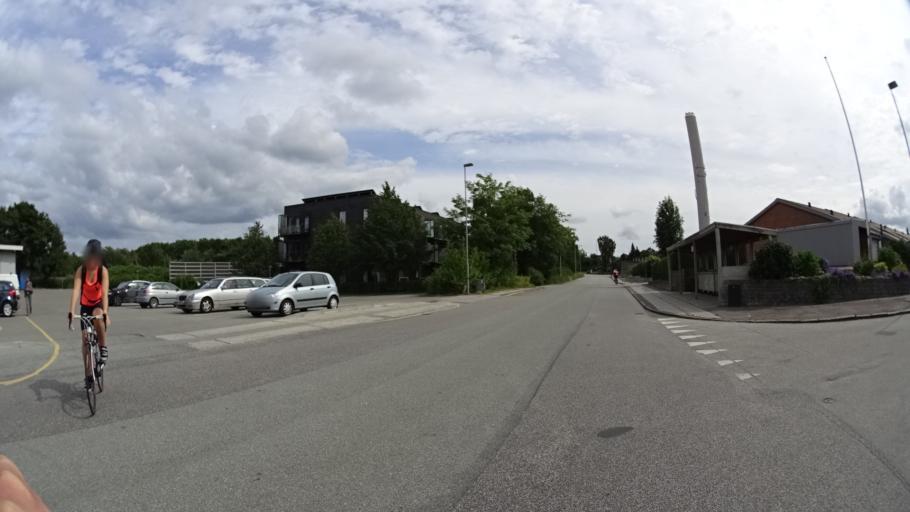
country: DK
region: Central Jutland
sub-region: Arhus Kommune
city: Arhus
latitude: 56.1375
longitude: 10.1725
